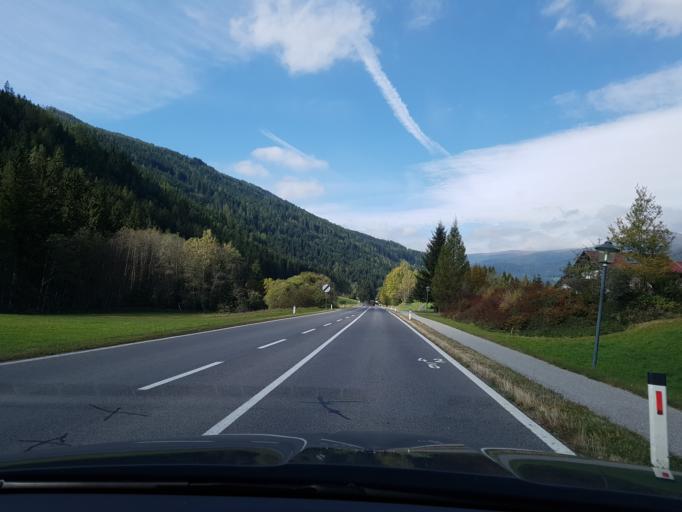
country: AT
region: Carinthia
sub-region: Politischer Bezirk Feldkirchen
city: Gnesau
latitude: 46.7970
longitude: 13.9107
